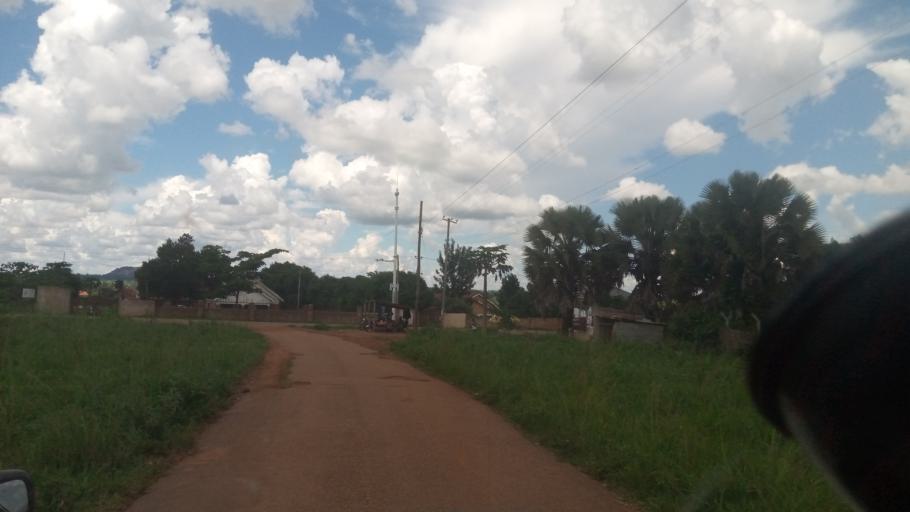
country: UG
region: Northern Region
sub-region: Lira District
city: Lira
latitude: 2.2404
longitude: 32.9082
